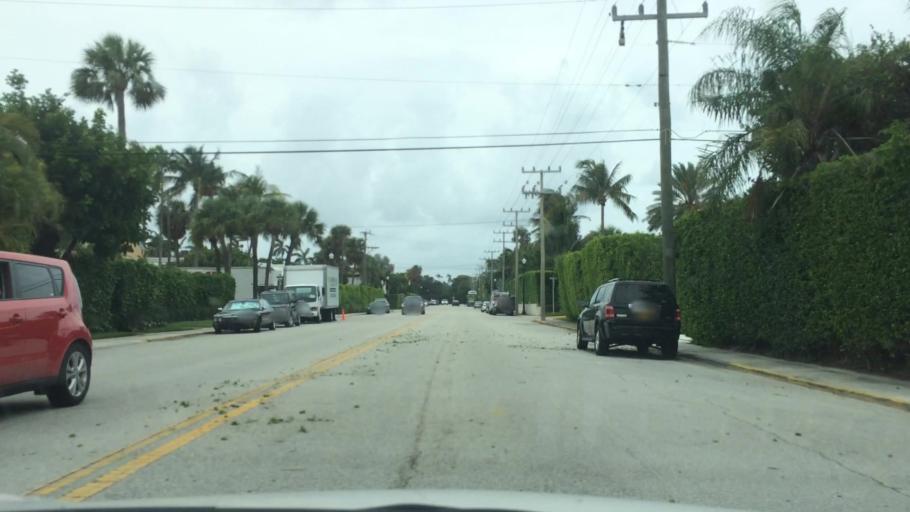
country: US
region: Florida
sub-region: Palm Beach County
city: Palm Beach
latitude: 26.7222
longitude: -80.0379
